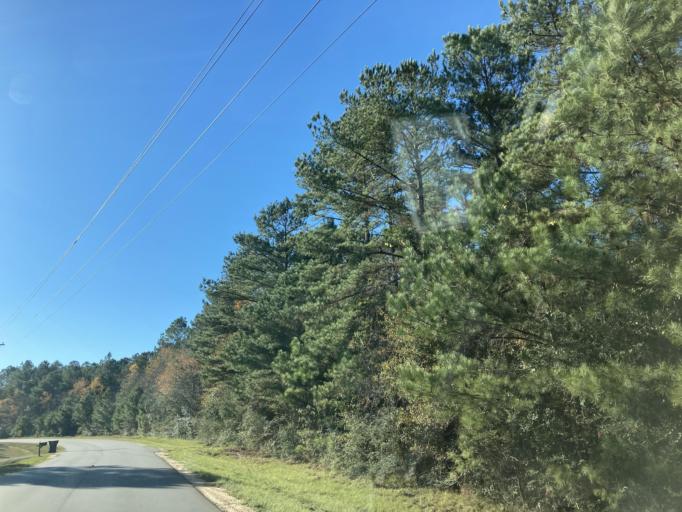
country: US
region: Mississippi
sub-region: Lamar County
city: Sumrall
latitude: 31.3747
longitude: -89.5824
